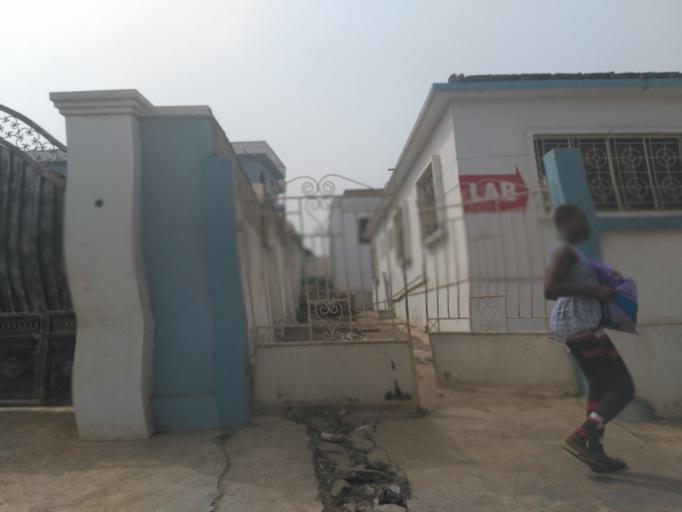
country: GH
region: Ashanti
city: Tafo
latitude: 6.7120
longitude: -1.6119
